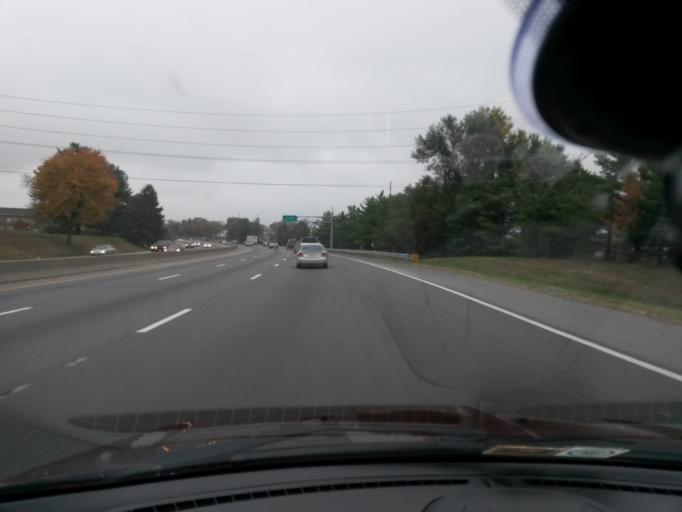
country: US
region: Virginia
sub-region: City of Roanoke
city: Roanoke
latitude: 37.2862
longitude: -79.9386
